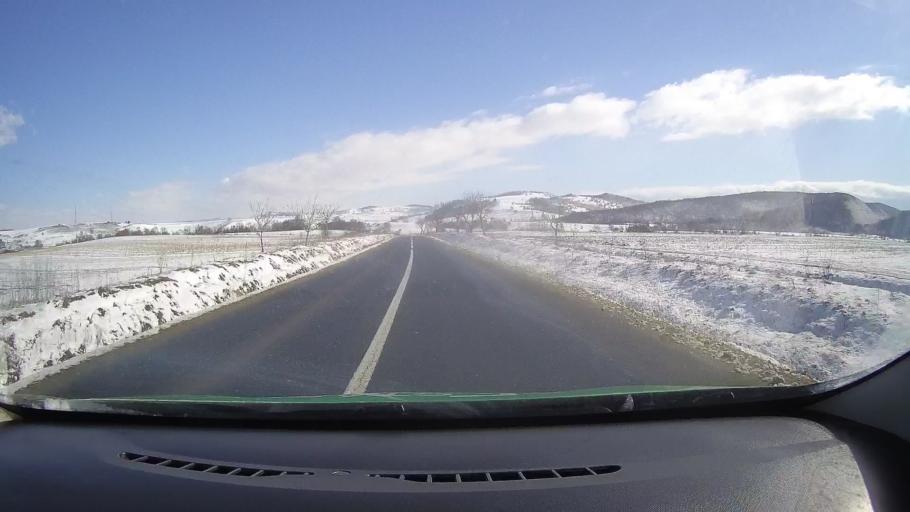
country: RO
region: Sibiu
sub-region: Comuna Rosia
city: Rosia
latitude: 45.7908
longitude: 24.3053
